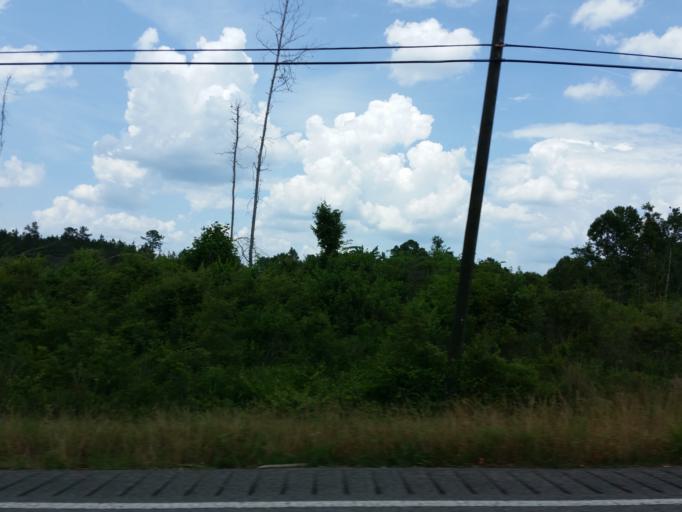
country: US
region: Alabama
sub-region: Sumter County
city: York
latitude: 32.4144
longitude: -88.2350
